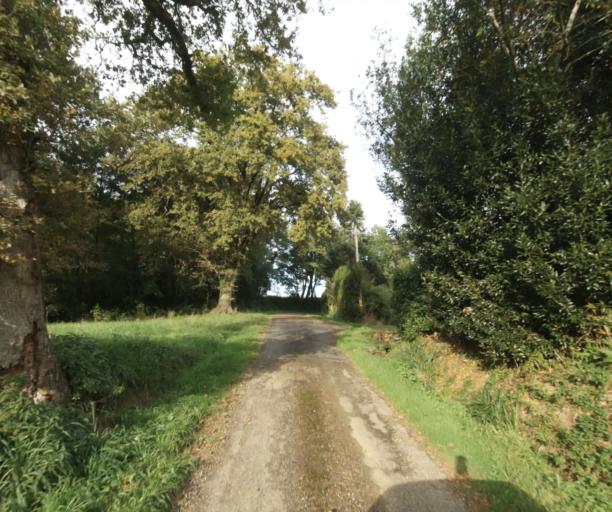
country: FR
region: Midi-Pyrenees
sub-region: Departement du Gers
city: Le Houga
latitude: 43.8488
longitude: -0.1486
